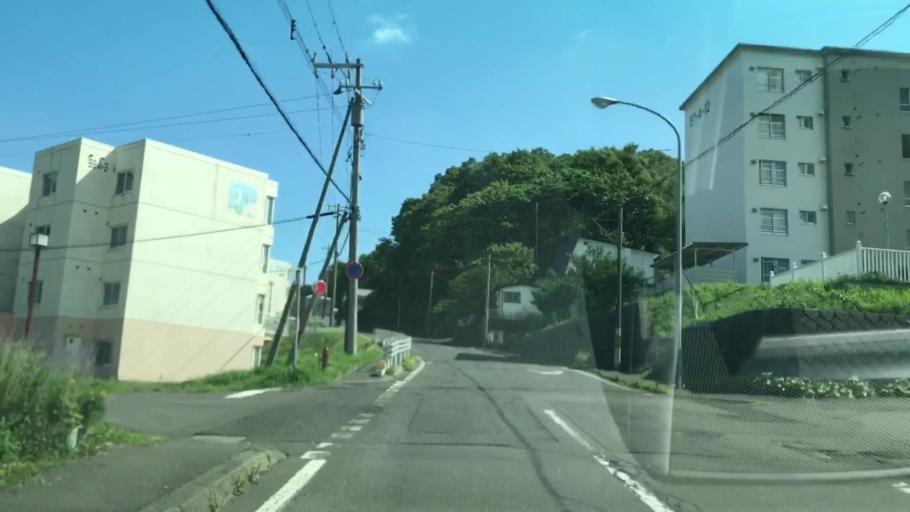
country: JP
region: Hokkaido
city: Muroran
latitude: 42.3071
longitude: 141.0009
